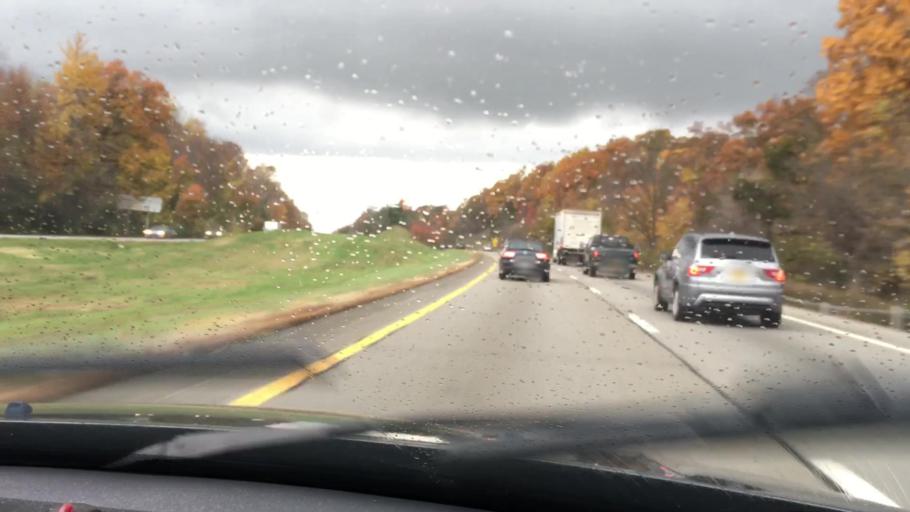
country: US
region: New York
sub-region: Dutchess County
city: Fishkill
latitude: 41.5297
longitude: -73.9221
